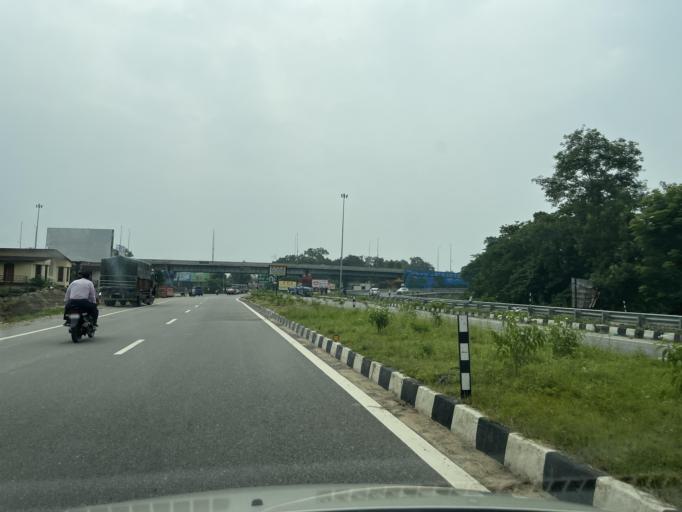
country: IN
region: Uttarakhand
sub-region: Dehradun
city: Raiwala
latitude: 30.0554
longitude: 78.2187
